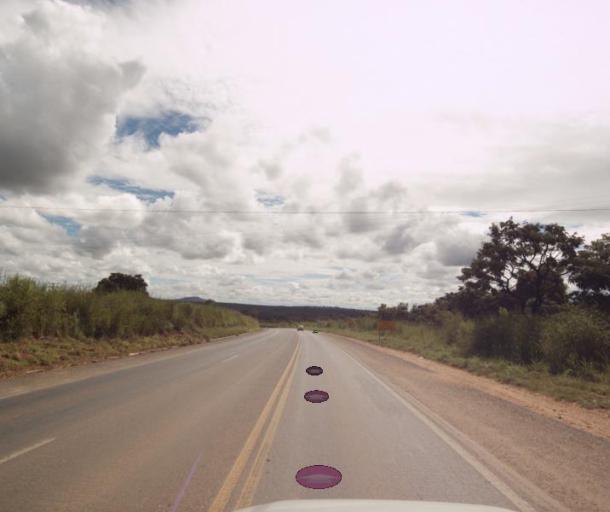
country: BR
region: Goias
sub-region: Uruacu
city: Uruacu
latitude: -14.5120
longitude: -49.1488
